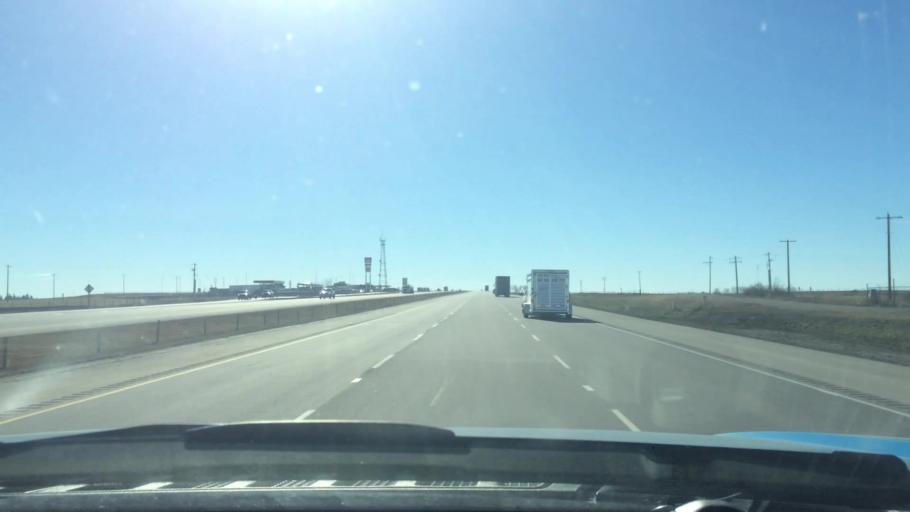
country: CA
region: Alberta
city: Crossfield
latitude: 51.4187
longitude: -114.0021
